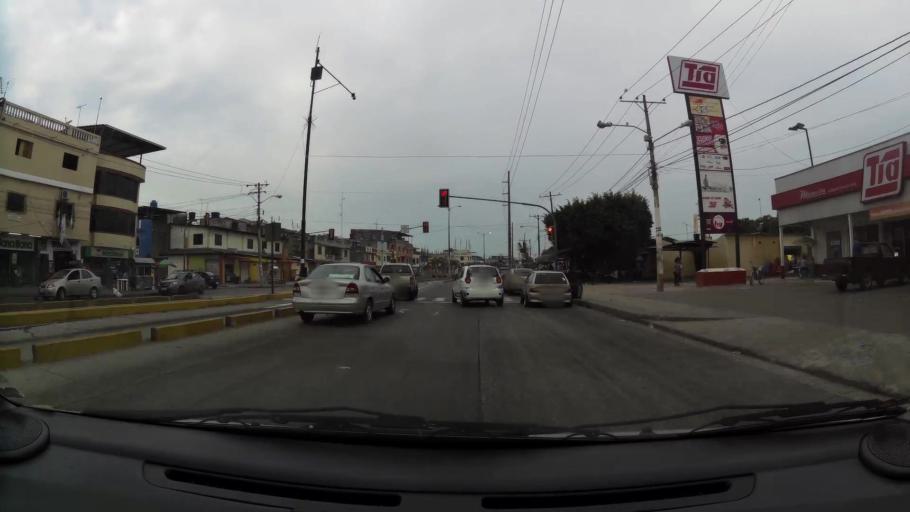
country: EC
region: Guayas
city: Guayaquil
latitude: -2.2511
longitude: -79.8848
